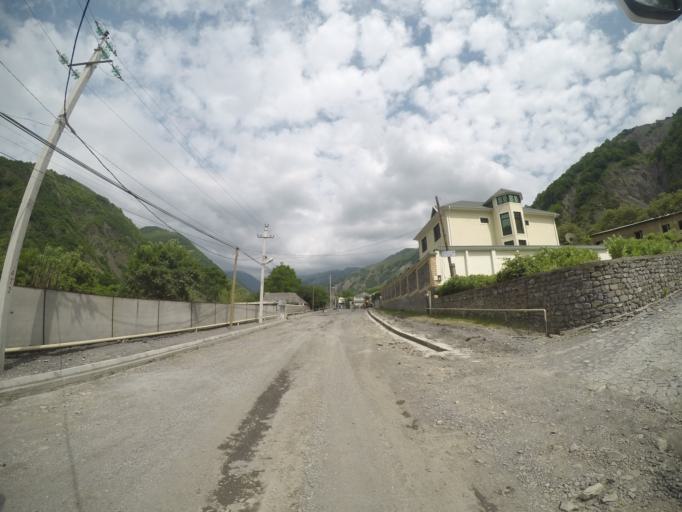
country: AZ
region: Qakh Rayon
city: Qaxbas
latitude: 41.4679
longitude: 47.0588
